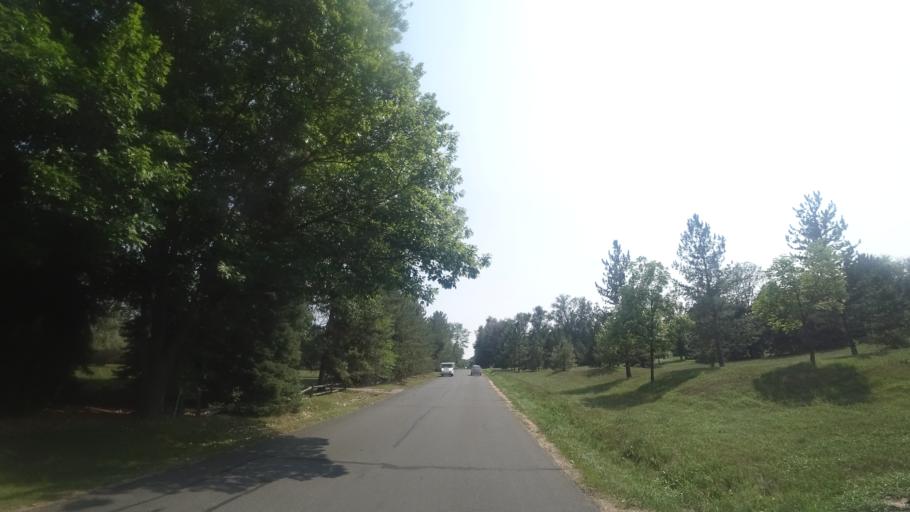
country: US
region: Colorado
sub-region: Arapahoe County
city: Cherry Hills Village
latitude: 39.6361
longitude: -104.9690
